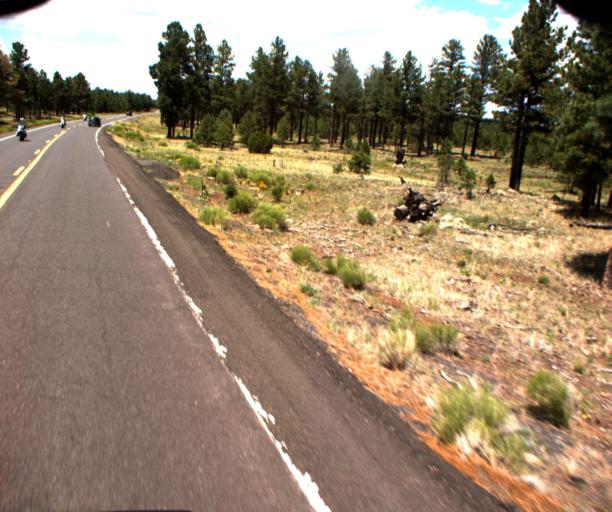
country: US
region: Arizona
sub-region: Coconino County
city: Parks
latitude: 35.4982
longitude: -111.8173
